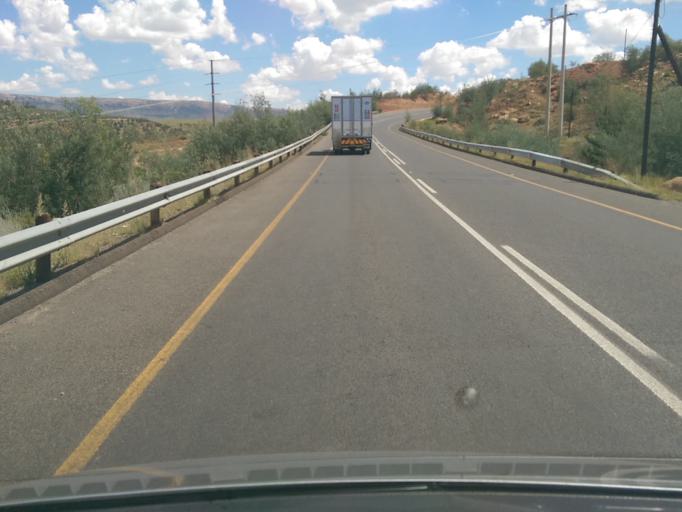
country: LS
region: Maseru
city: Maseru
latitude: -29.3997
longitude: 27.5326
